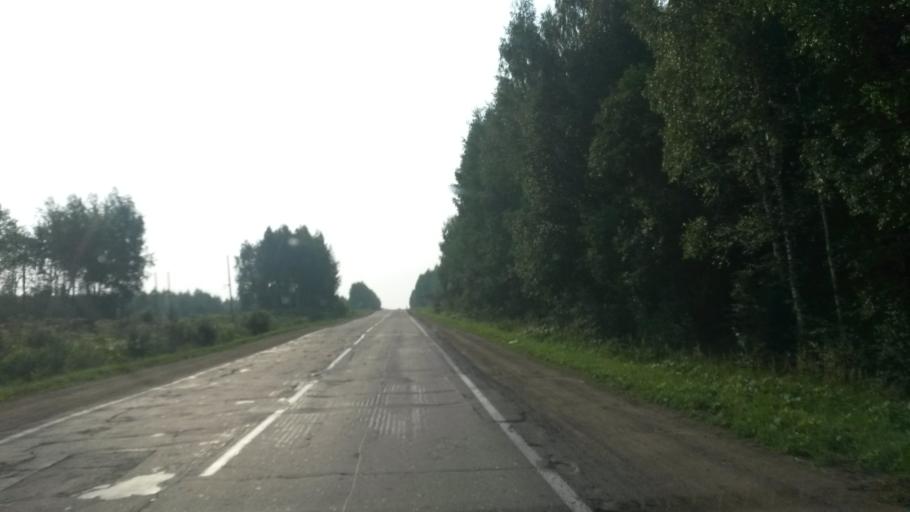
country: RU
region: Jaroslavl
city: Dubki
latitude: 57.2512
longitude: 40.1175
